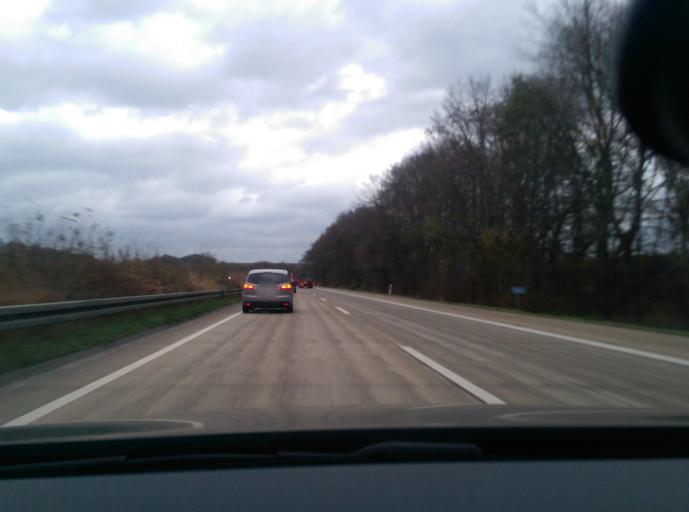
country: DE
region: Lower Saxony
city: Kalefeld
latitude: 51.8121
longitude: 10.1008
